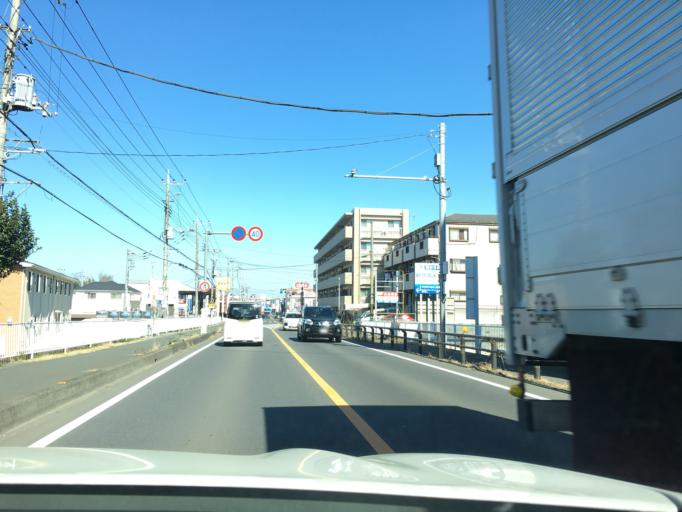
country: JP
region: Saitama
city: Kamifukuoka
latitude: 35.8731
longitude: 139.5031
